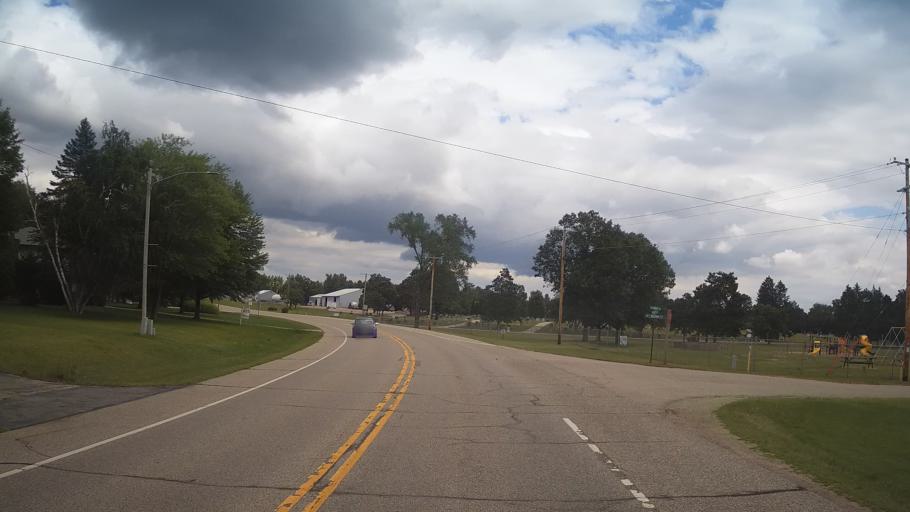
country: US
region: Wisconsin
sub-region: Marquette County
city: Westfield
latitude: 44.0356
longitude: -89.5180
